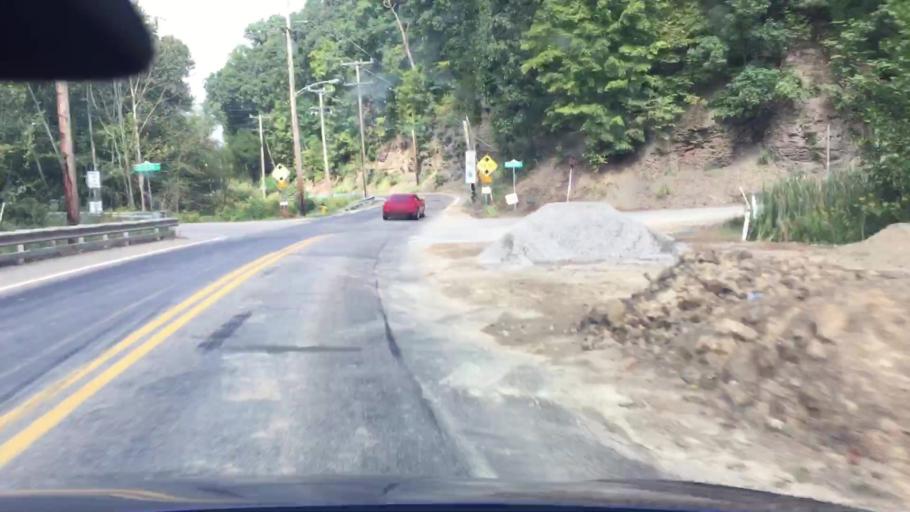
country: US
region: Pennsylvania
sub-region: Allegheny County
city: Cheswick
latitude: 40.5742
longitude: -79.8220
